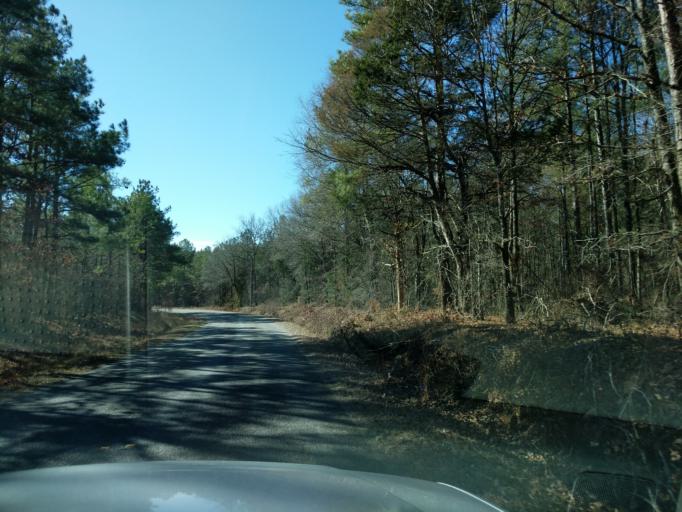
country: US
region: South Carolina
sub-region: Saluda County
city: Saluda
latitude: 34.0447
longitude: -81.8257
